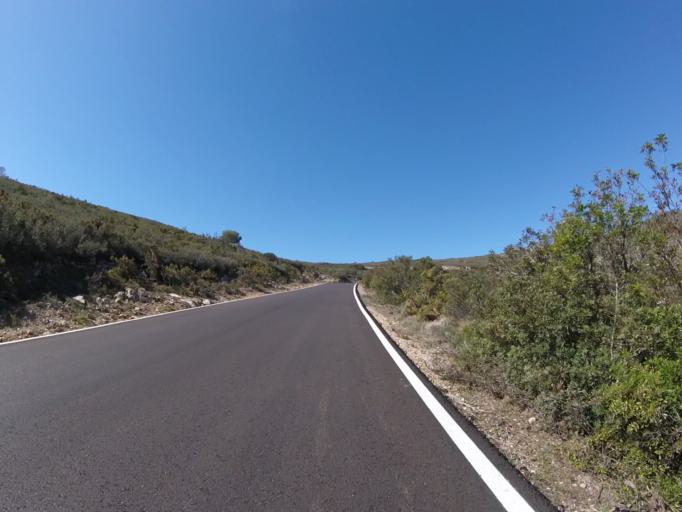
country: ES
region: Valencia
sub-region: Provincia de Castello
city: Cervera del Maestre
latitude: 40.4064
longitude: 0.2231
